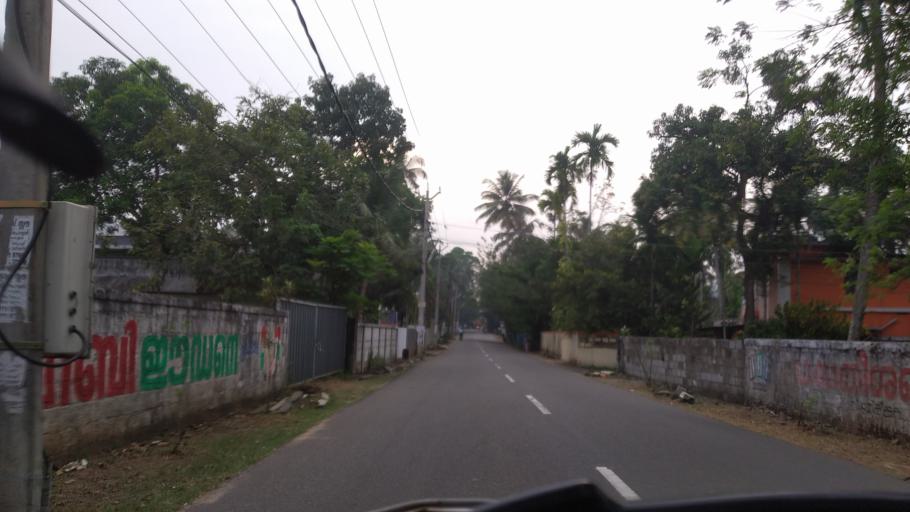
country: IN
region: Kerala
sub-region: Ernakulam
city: Elur
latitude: 10.1341
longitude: 76.2452
